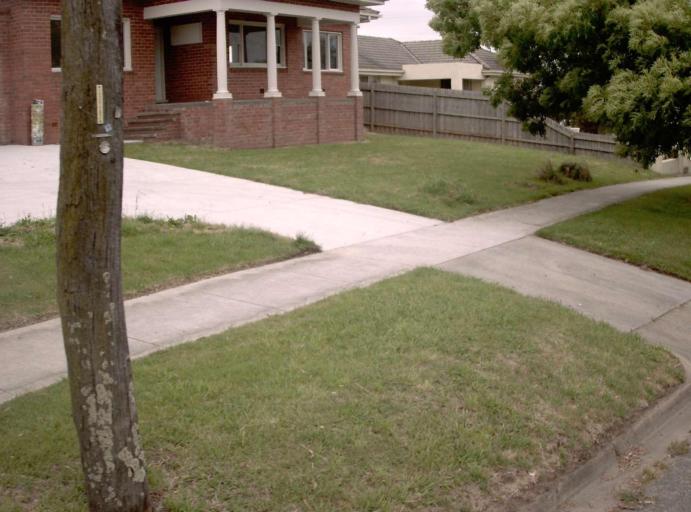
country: AU
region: Victoria
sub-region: Bass Coast
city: North Wonthaggi
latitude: -38.4365
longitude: 145.8276
